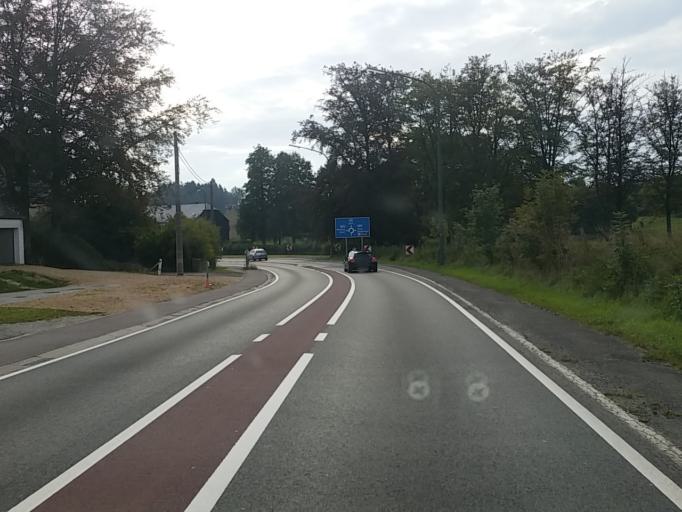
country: BE
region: Wallonia
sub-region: Province du Luxembourg
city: Tintigny
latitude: 49.6841
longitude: 5.5071
